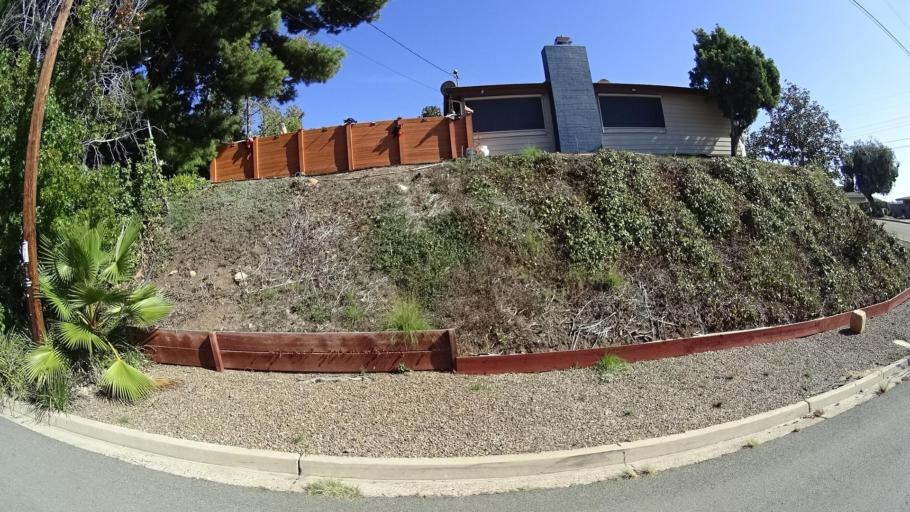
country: US
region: California
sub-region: San Diego County
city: Casa de Oro-Mount Helix
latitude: 32.7557
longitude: -116.9782
